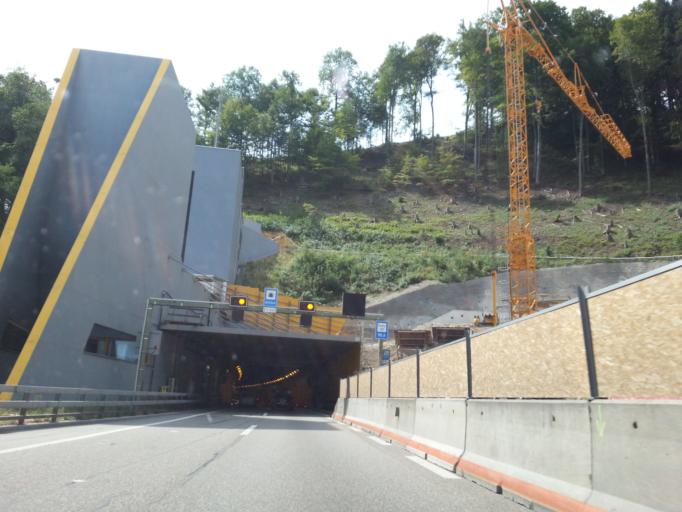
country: CH
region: Basel-Landschaft
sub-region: Bezirk Waldenburg
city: Diegten
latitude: 47.3792
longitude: 7.8163
